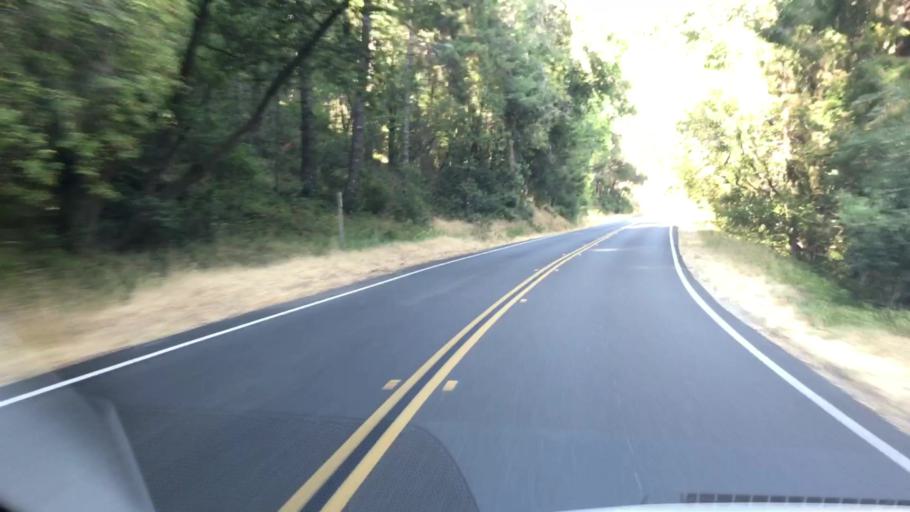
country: US
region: California
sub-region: Marin County
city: Lagunitas-Forest Knolls
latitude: 38.0297
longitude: -122.7411
